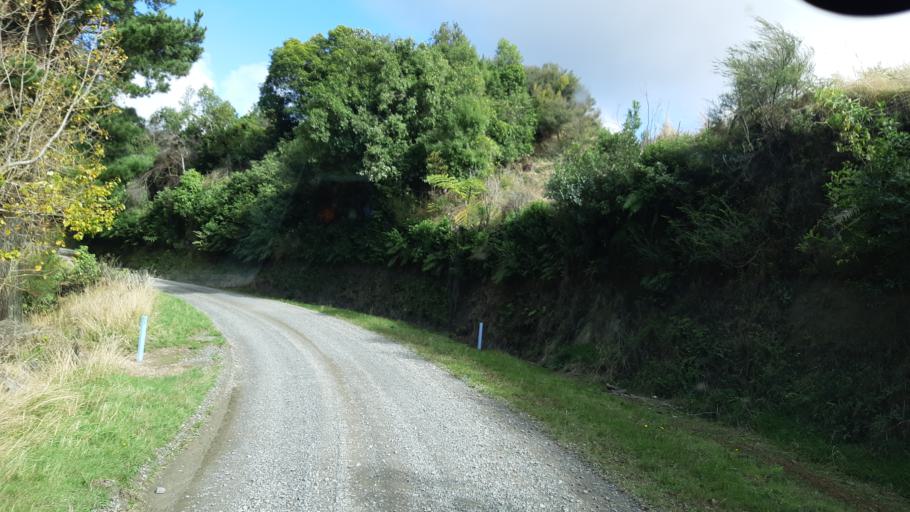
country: NZ
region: Manawatu-Wanganui
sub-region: Ruapehu District
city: Waiouru
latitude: -39.8157
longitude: 175.6628
